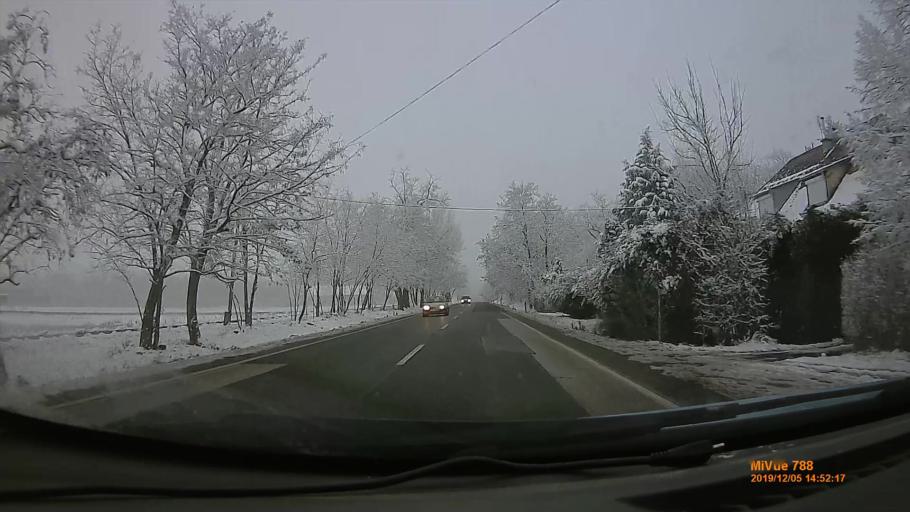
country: HU
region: Szabolcs-Szatmar-Bereg
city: Nyirtelek
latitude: 47.9999
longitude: 21.6465
